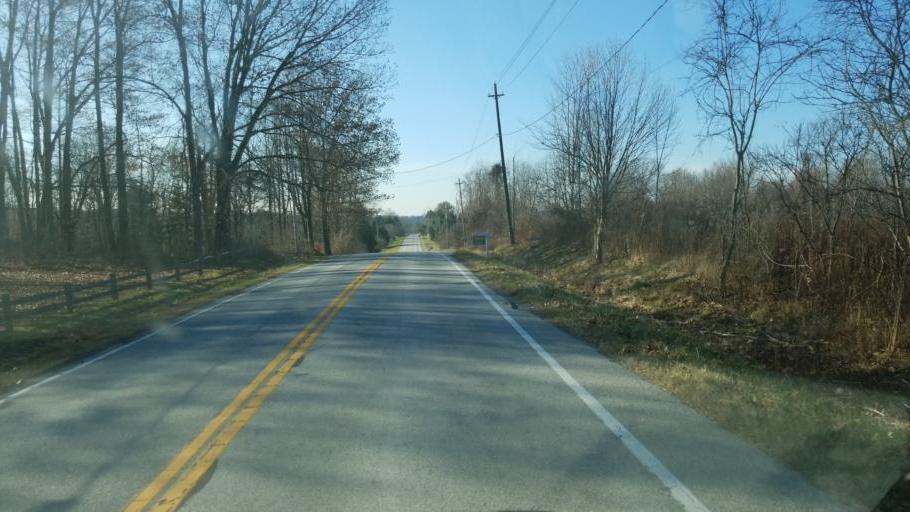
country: US
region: Ohio
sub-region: Geauga County
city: Burton
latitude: 41.4945
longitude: -81.2056
